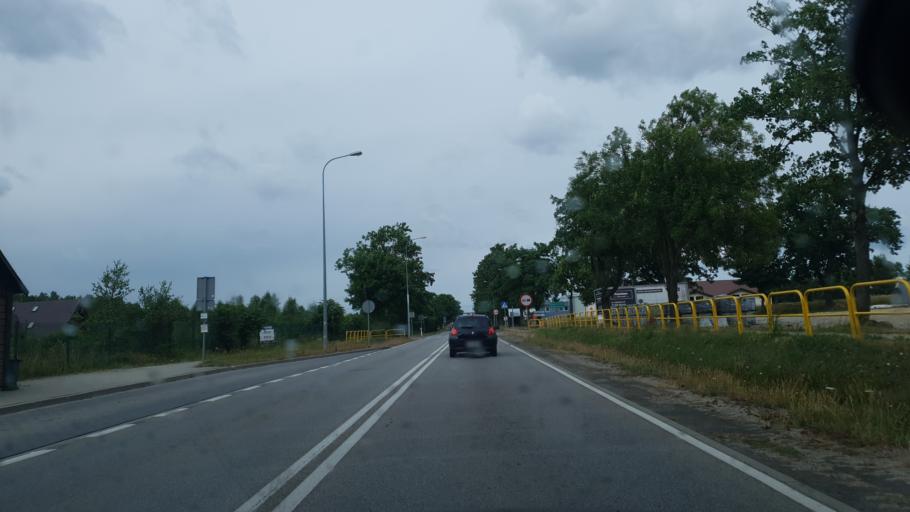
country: PL
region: Pomeranian Voivodeship
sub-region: Powiat kartuski
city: Banino
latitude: 54.4099
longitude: 18.3702
